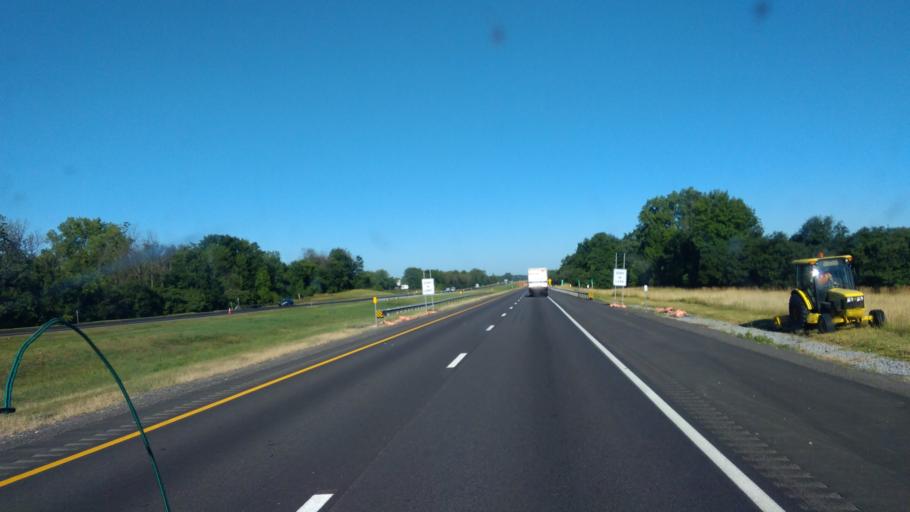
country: US
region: New York
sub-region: Ontario County
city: Clifton Springs
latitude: 42.9744
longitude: -77.1101
